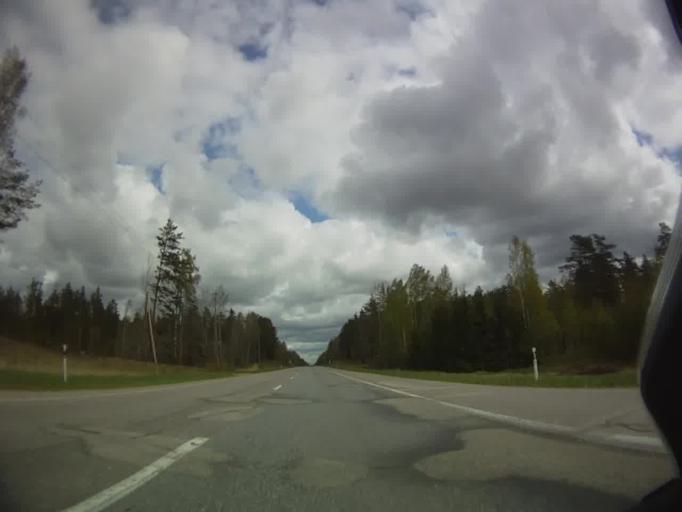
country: LV
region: Incukalns
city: Vangazi
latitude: 57.0988
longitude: 24.5818
